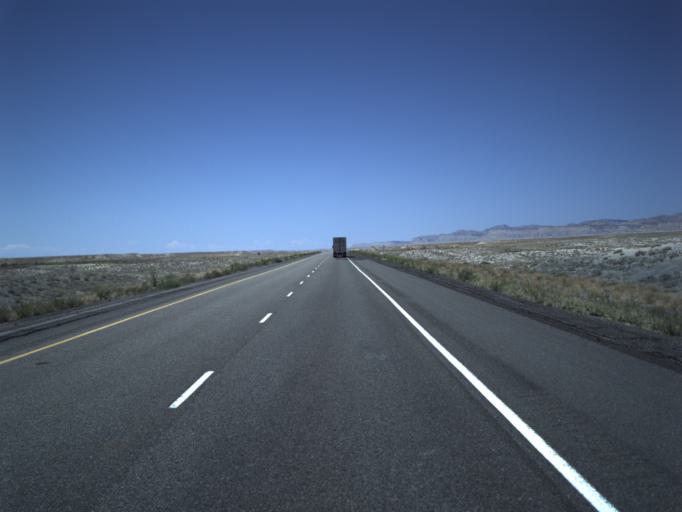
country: US
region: Utah
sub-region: Grand County
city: Moab
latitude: 38.9370
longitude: -109.4724
